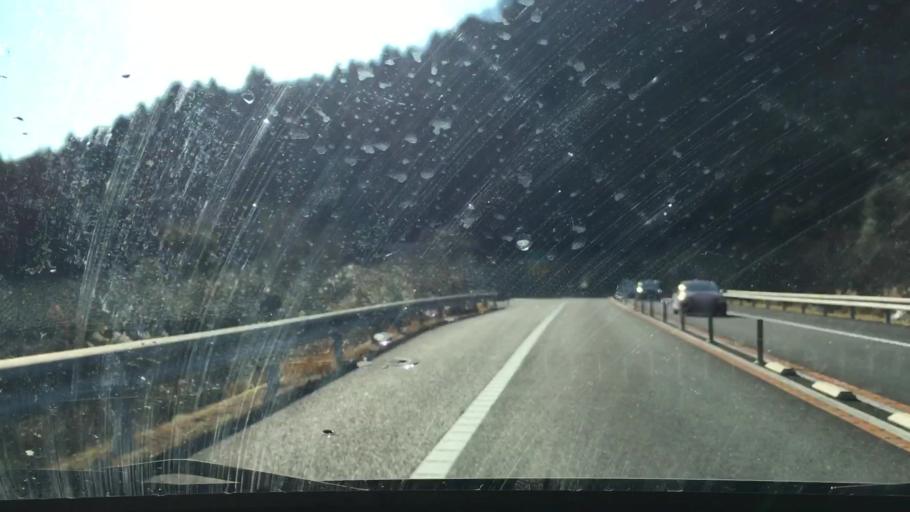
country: JP
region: Kagoshima
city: Kokubu-matsuki
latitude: 31.7320
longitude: 130.8375
